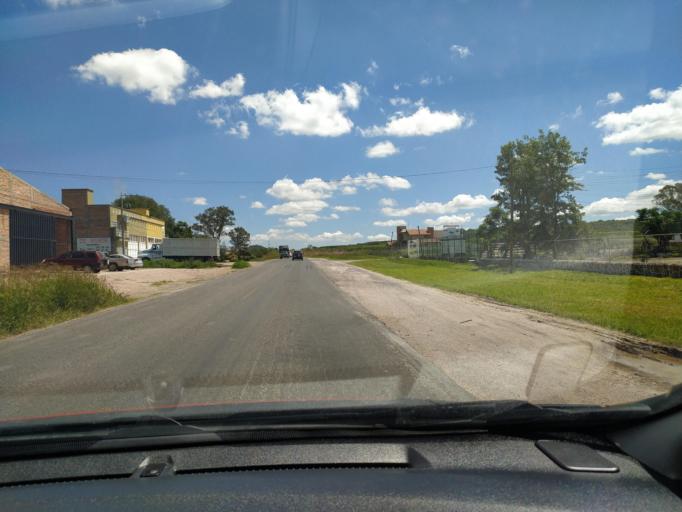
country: MX
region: Jalisco
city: San Julian
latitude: 21.0070
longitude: -102.1417
